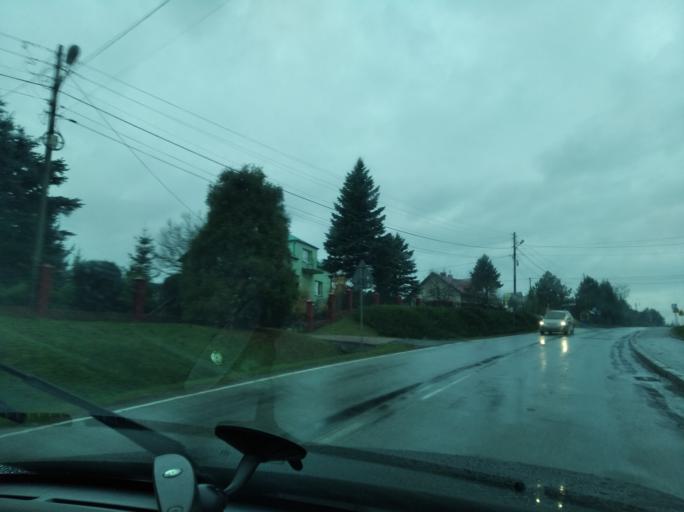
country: PL
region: Subcarpathian Voivodeship
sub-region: Powiat lancucki
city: Lancut
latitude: 50.0416
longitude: 22.2290
